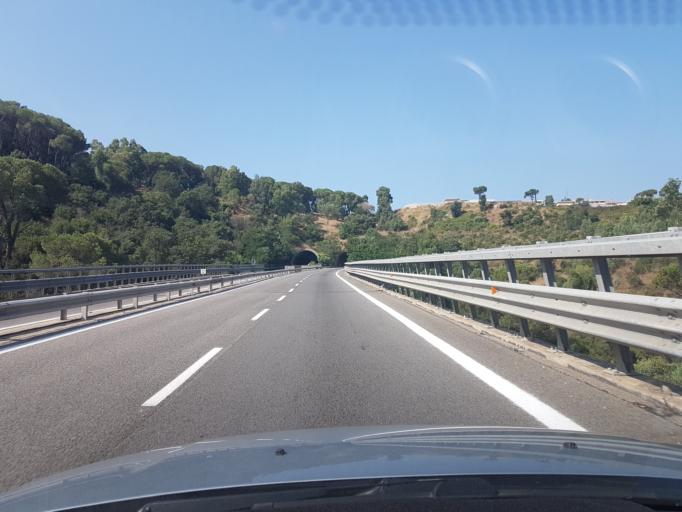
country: IT
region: Sardinia
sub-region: Provincia di Nuoro
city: Nuoro
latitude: 40.3312
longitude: 9.2925
